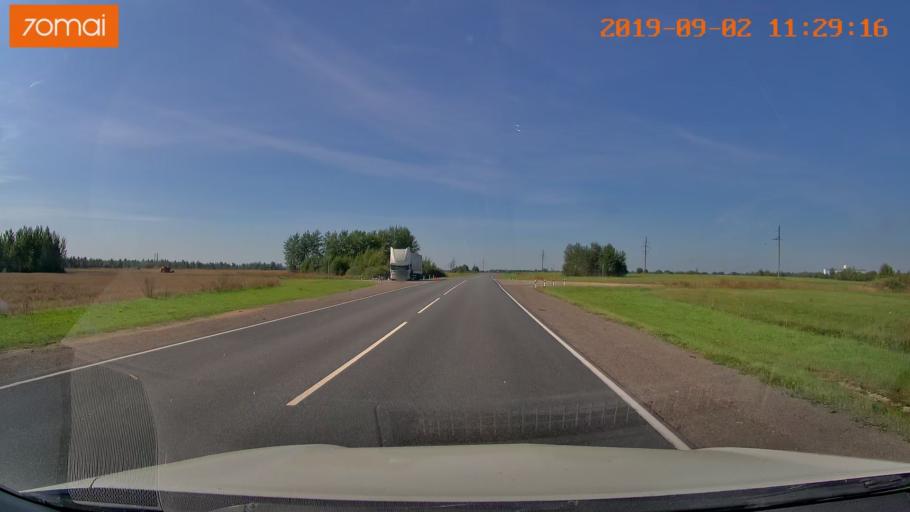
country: RU
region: Smolensk
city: Roslavl'
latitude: 53.9900
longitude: 32.8683
